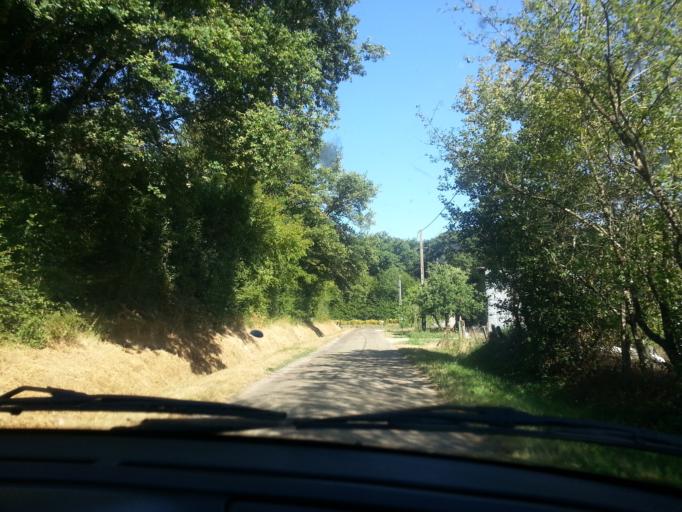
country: FR
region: Bourgogne
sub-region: Departement de Saone-et-Loire
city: Saint-Martin-en-Bresse
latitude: 46.7677
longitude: 5.0601
